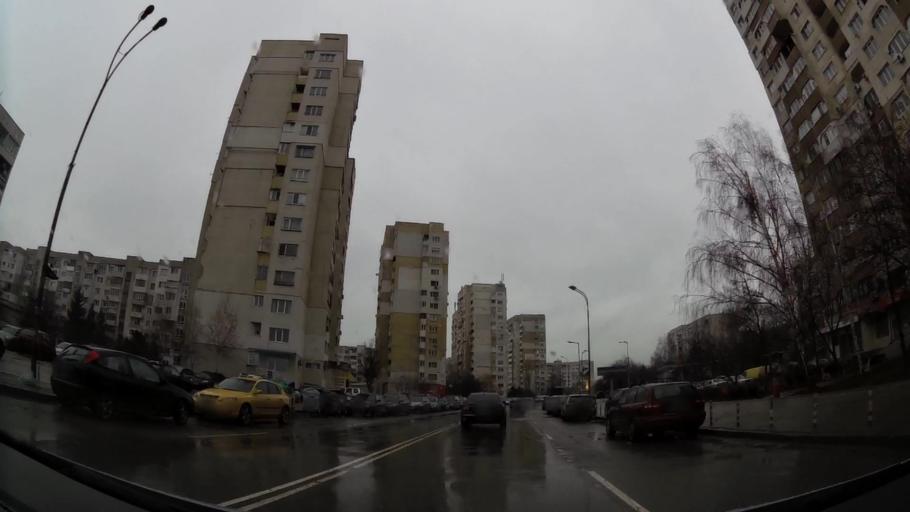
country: BG
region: Sofia-Capital
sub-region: Stolichna Obshtina
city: Sofia
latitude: 42.6398
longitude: 23.3817
